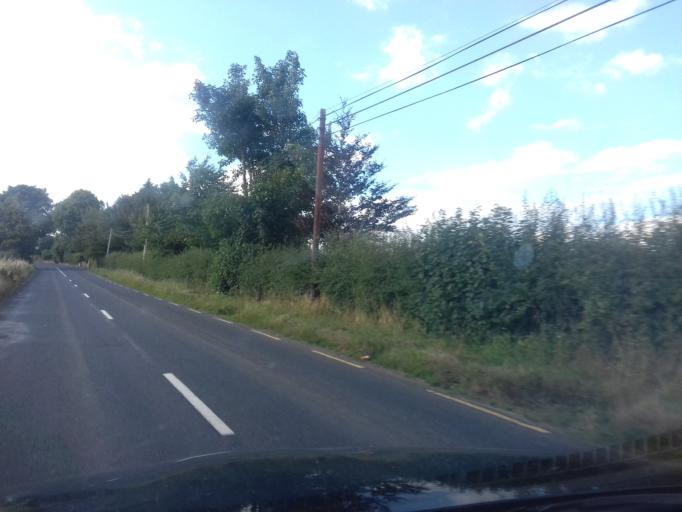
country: IE
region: Leinster
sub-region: Loch Garman
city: New Ross
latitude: 52.4427
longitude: -6.9611
